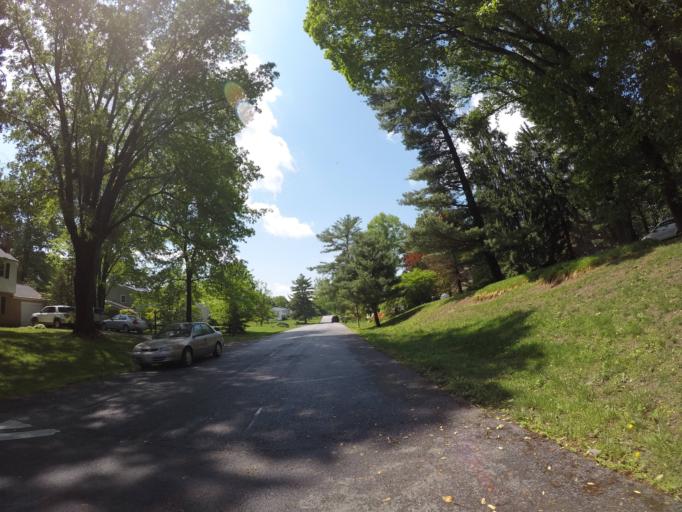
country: US
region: Maryland
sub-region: Howard County
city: Columbia
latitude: 39.2883
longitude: -76.8415
